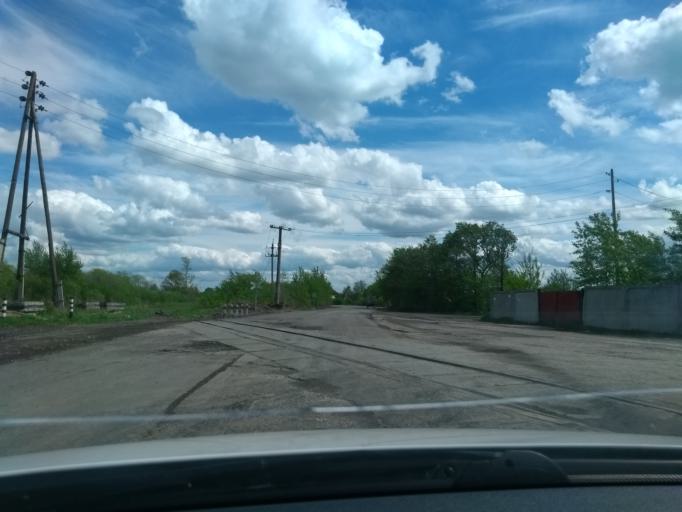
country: RU
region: Perm
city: Kondratovo
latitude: 58.0108
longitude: 56.0751
